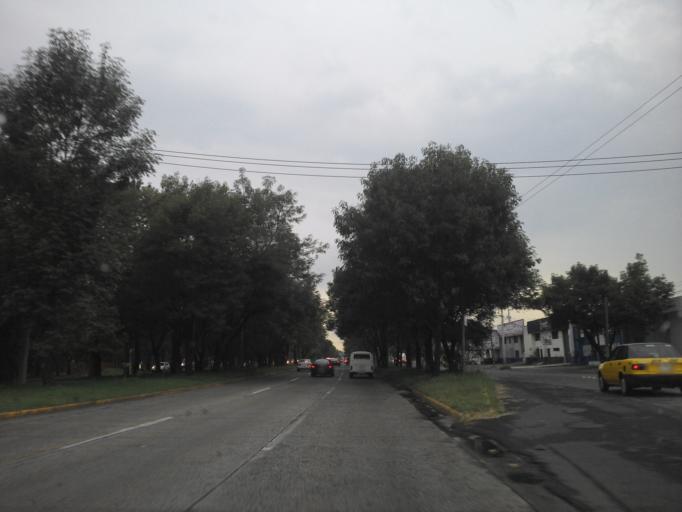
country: MX
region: Jalisco
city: Tlaquepaque
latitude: 20.6383
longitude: -103.3446
